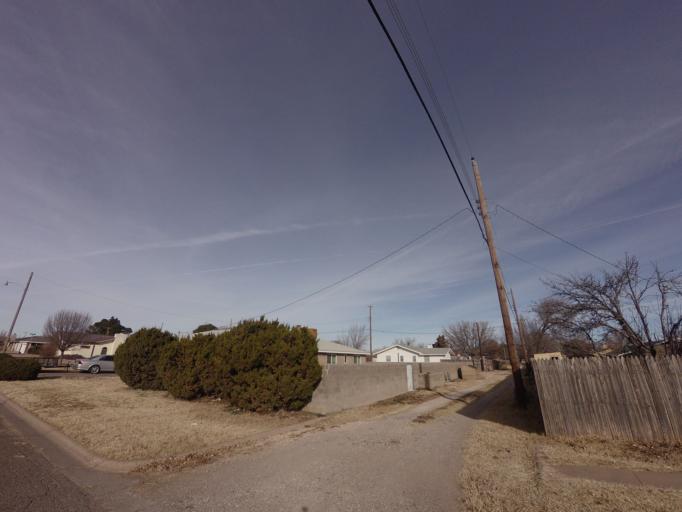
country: US
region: New Mexico
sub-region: Curry County
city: Clovis
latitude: 34.4157
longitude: -103.2234
